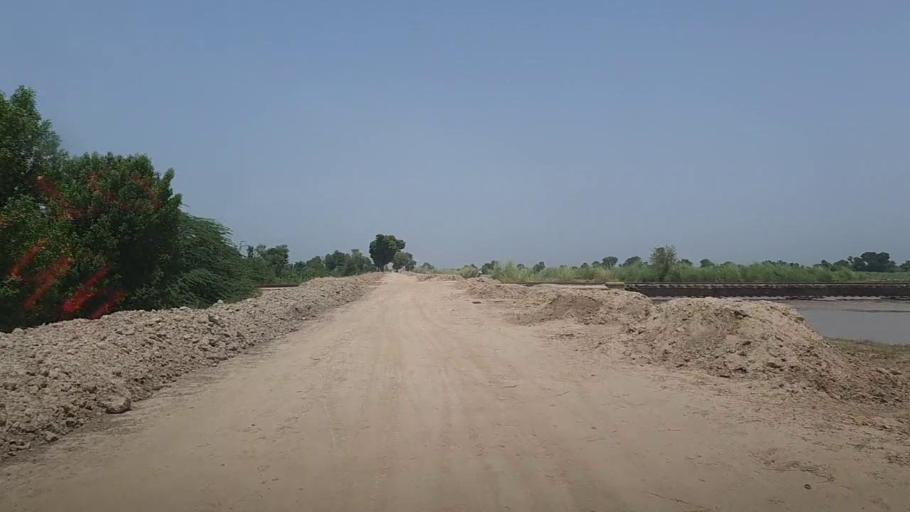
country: PK
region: Sindh
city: Pad Idan
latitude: 26.7906
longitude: 68.2761
